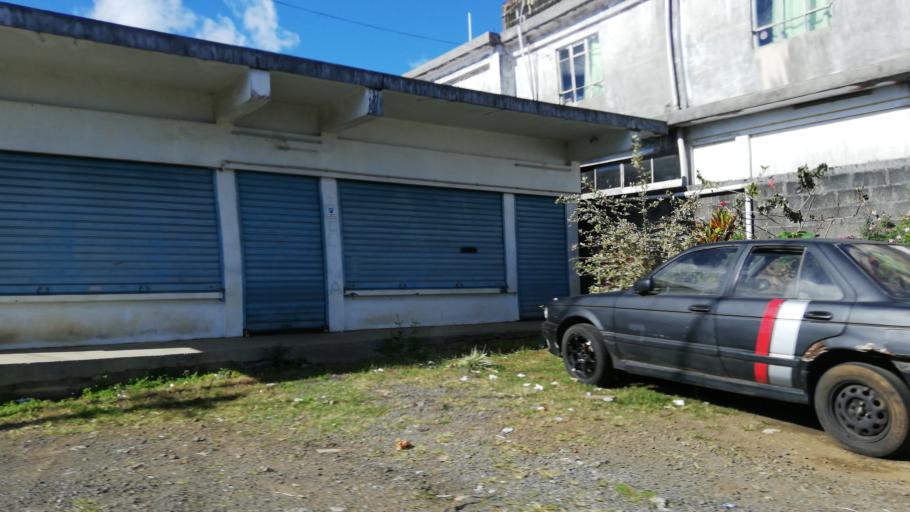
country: MU
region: Moka
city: Quartier Militaire
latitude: -20.2454
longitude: 57.5982
